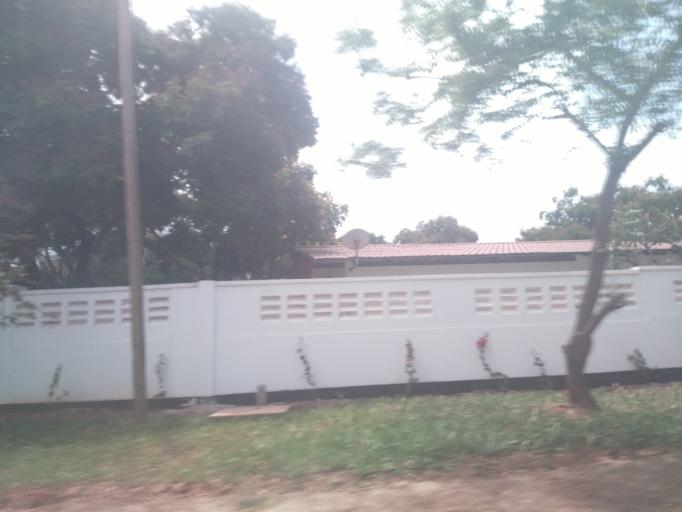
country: TZ
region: Dar es Salaam
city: Magomeni
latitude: -6.7541
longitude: 39.2799
